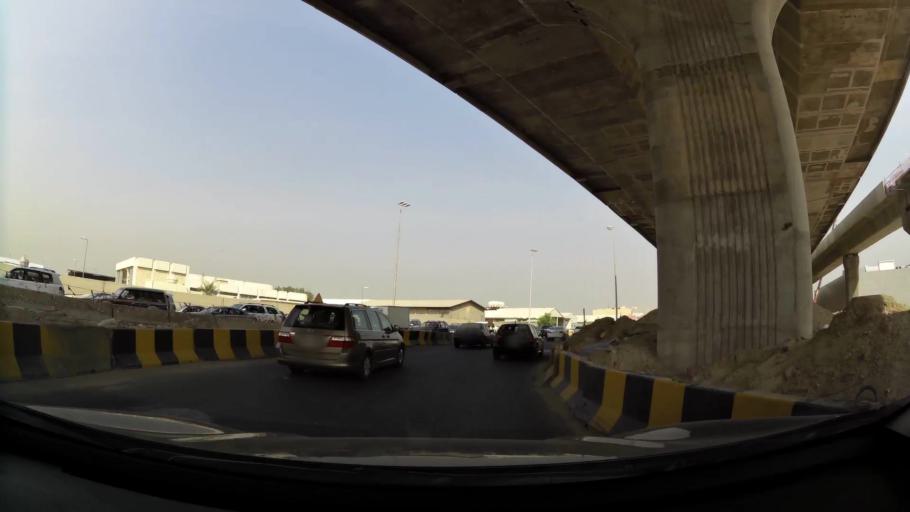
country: KW
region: Al Asimah
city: Ash Shamiyah
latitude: 29.3324
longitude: 47.9317
